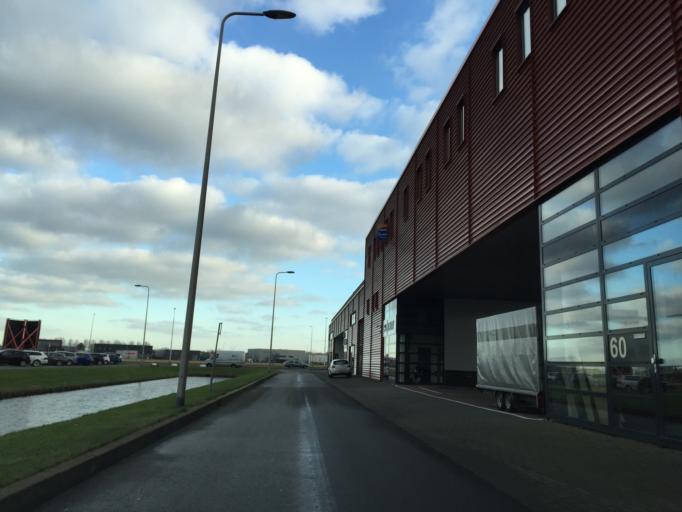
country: NL
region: South Holland
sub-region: Gemeente Lansingerland
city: Berkel en Rodenrijs
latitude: 51.9802
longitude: 4.4465
